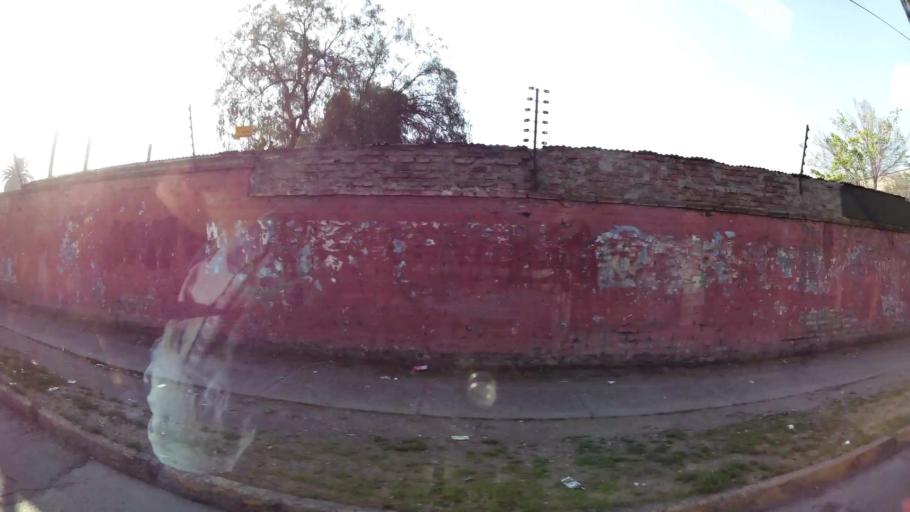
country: CL
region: Santiago Metropolitan
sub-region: Provincia de Santiago
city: Santiago
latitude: -33.4130
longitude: -70.6373
